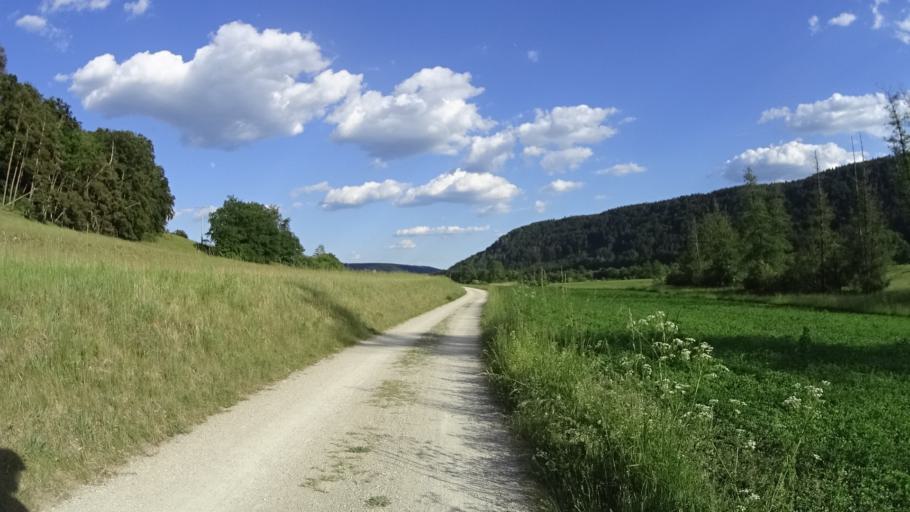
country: DE
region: Bavaria
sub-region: Upper Palatinate
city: Dietfurt
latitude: 49.0186
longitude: 11.6035
